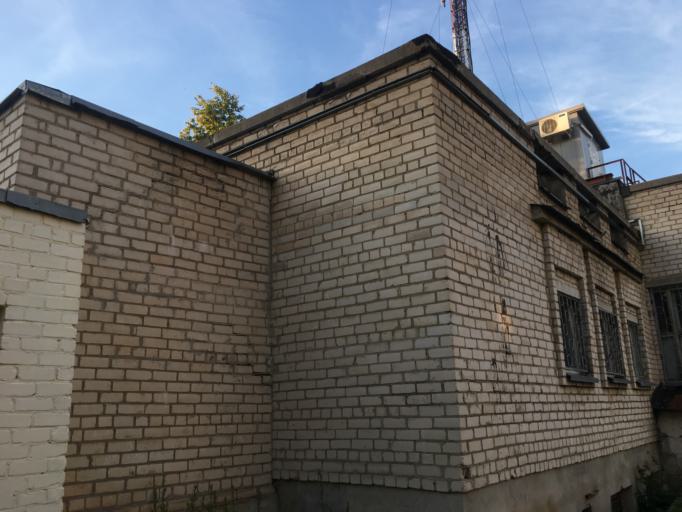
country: BY
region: Grodnenskaya
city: Hrodna
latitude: 53.7023
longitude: 23.7989
